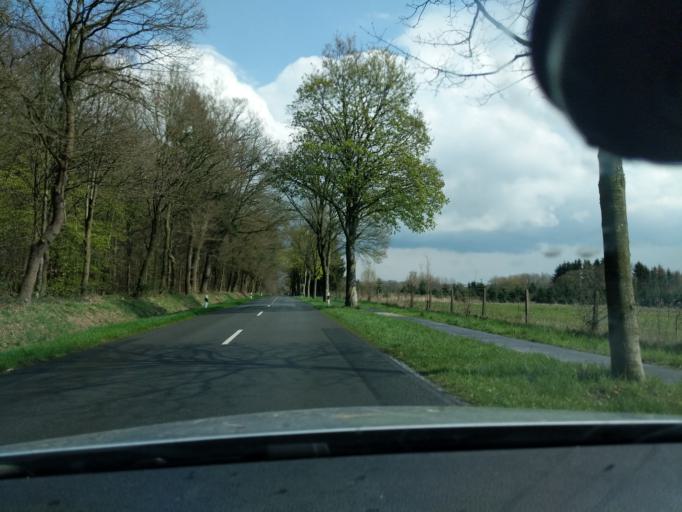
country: DE
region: Lower Saxony
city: Harsefeld
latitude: 53.4621
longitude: 9.4932
